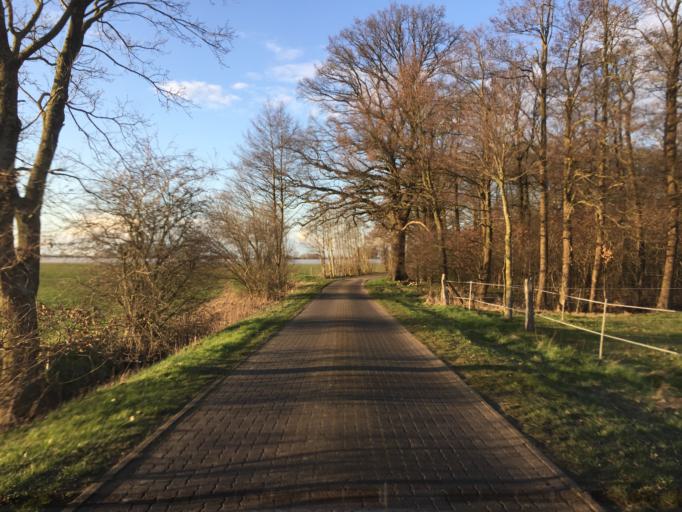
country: DE
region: Lower Saxony
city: Kirchdorf
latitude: 52.6110
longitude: 8.8823
